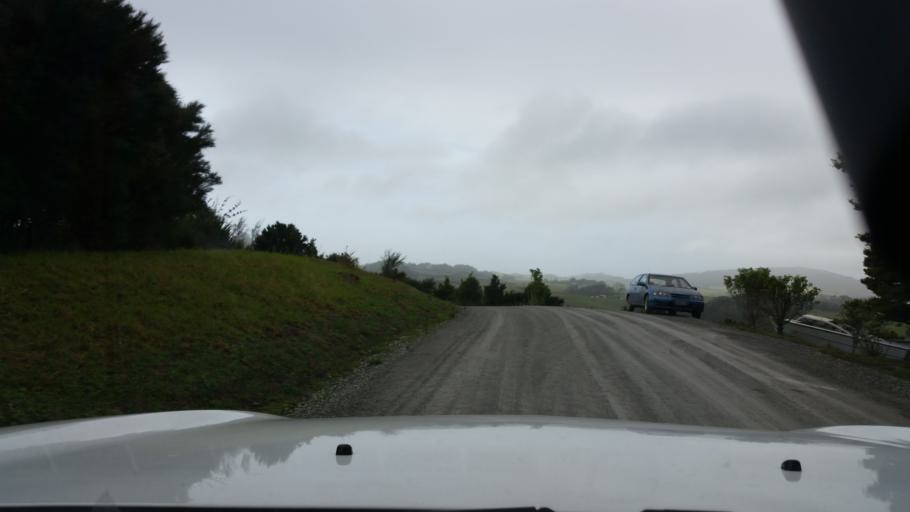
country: NZ
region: Northland
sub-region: Whangarei
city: Ngunguru
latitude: -35.7371
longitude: 174.4931
